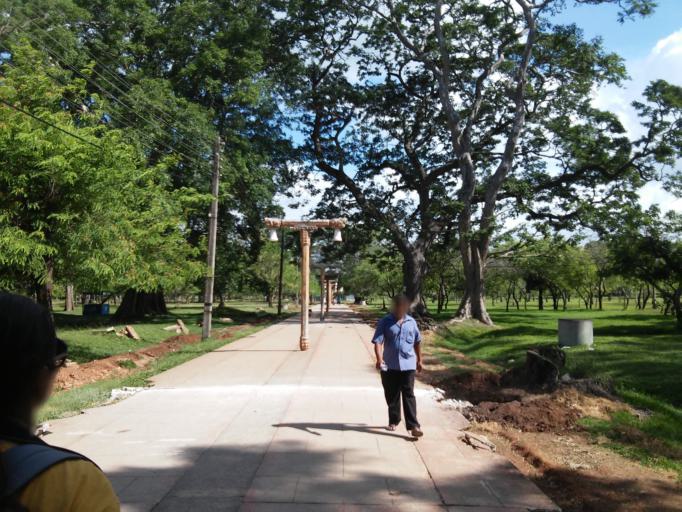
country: LK
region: North Central
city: Anuradhapura
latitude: 8.3494
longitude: 80.3978
